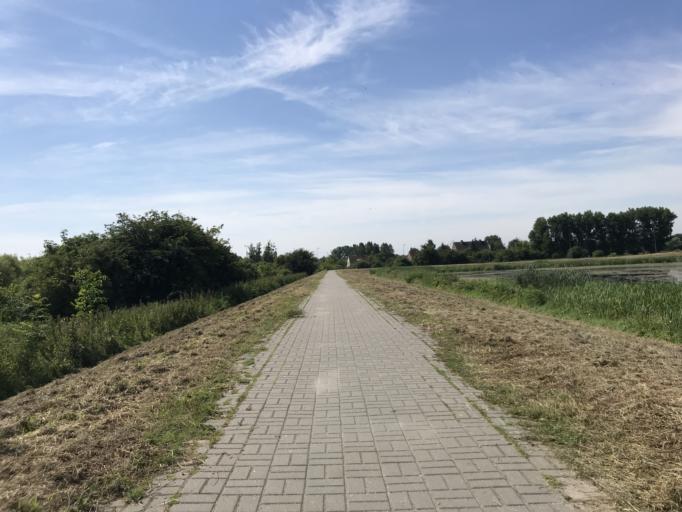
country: PL
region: Pomeranian Voivodeship
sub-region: Gdansk
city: Gdansk
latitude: 54.3385
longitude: 18.6609
